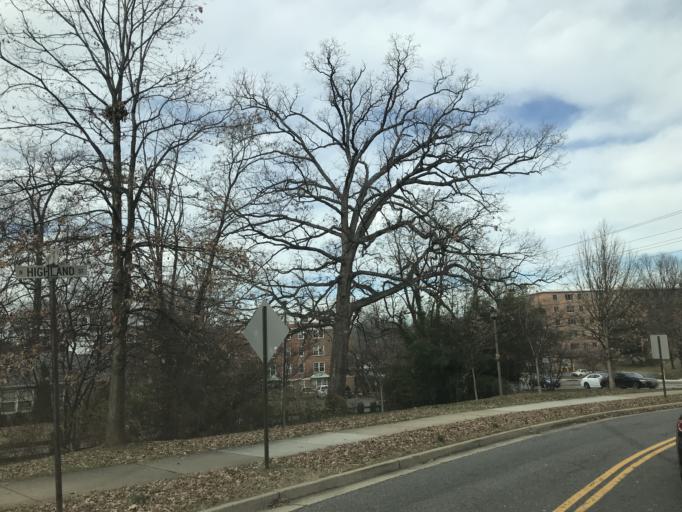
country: US
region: Virginia
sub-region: Arlington County
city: Arlington
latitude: 38.8943
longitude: -77.0944
